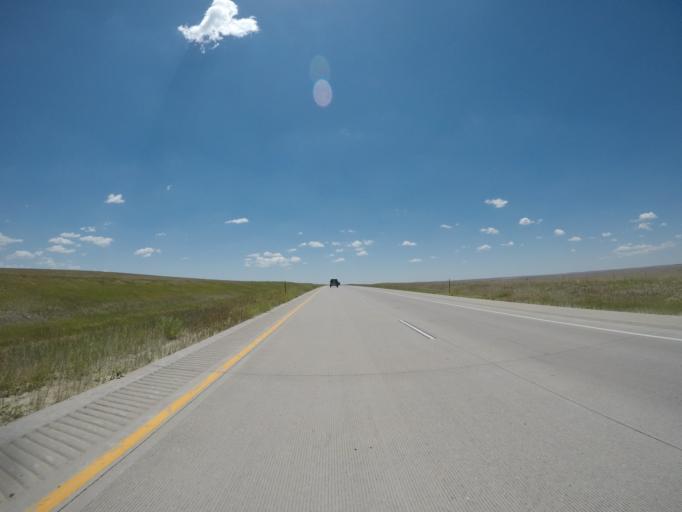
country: US
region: Colorado
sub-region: Lincoln County
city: Limon
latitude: 39.3931
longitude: -103.8952
